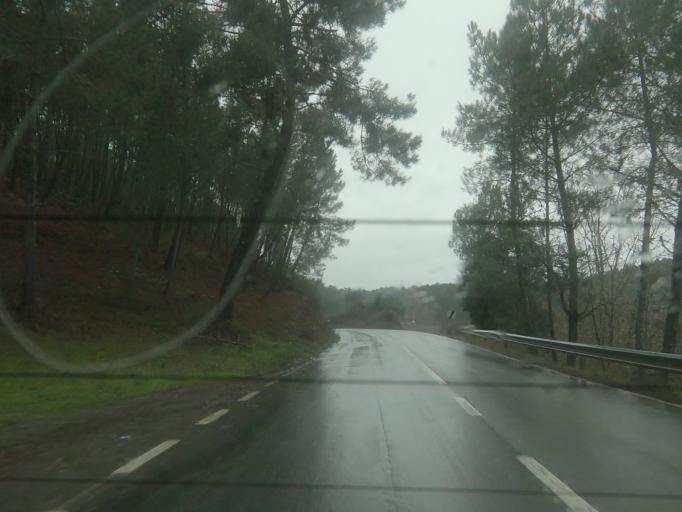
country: PT
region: Vila Real
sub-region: Vila Real
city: Vila Real
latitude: 41.2561
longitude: -7.6854
